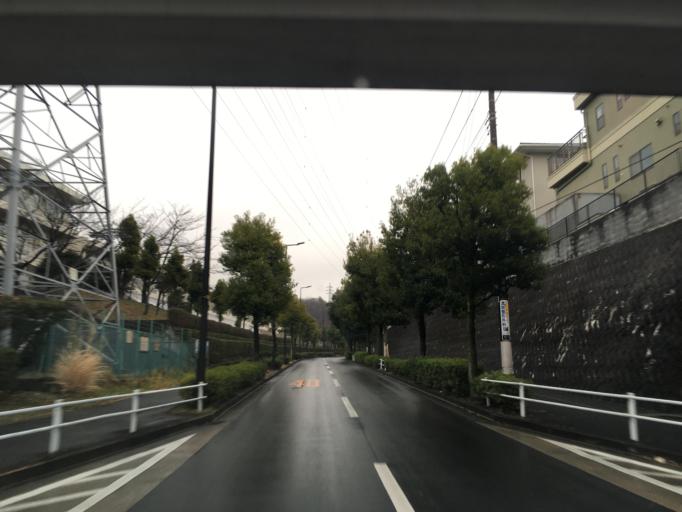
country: JP
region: Tokyo
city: Hino
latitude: 35.6369
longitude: 139.4562
